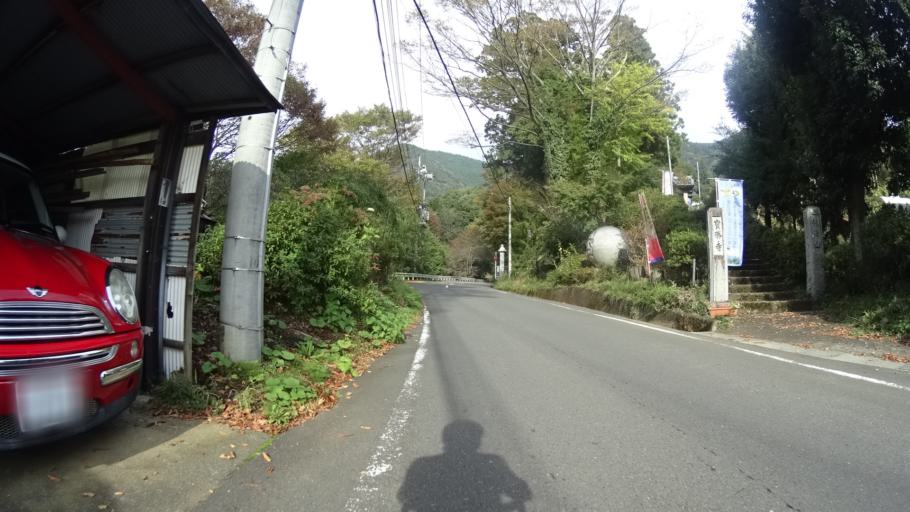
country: JP
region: Yamanashi
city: Uenohara
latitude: 35.6258
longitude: 139.0322
